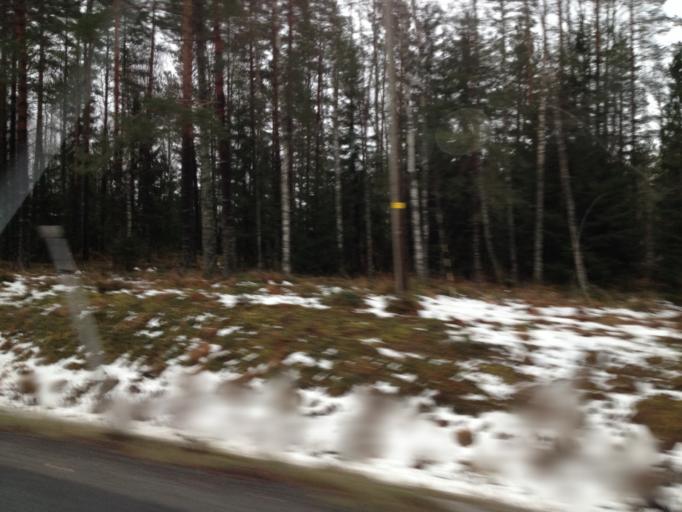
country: FI
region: Uusimaa
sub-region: Raaseporin
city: Ekenaes
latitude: 59.9484
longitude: 23.3557
